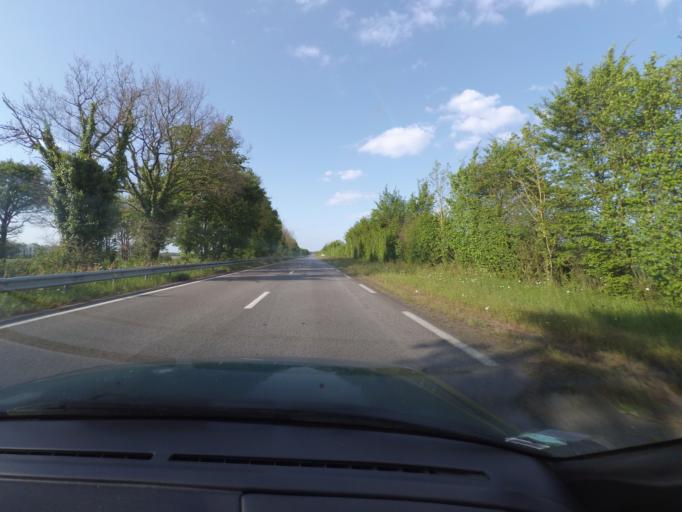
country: FR
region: Pays de la Loire
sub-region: Departement de la Vendee
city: Saligny
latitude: 46.8475
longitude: -1.4145
